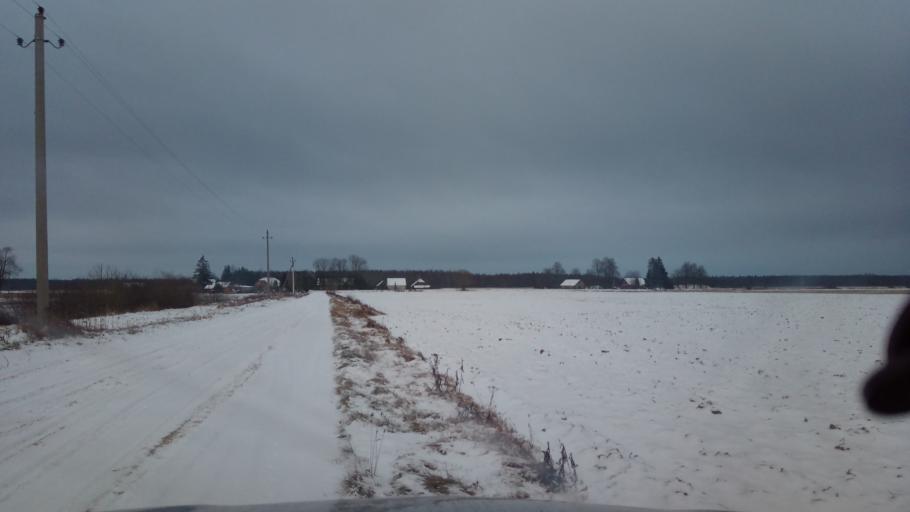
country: LT
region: Vilnius County
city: Ukmerge
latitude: 55.4784
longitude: 24.6260
